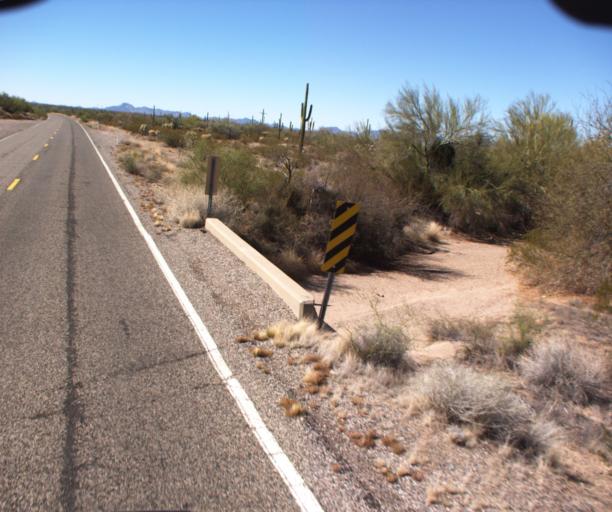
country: US
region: Arizona
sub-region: Pima County
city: Ajo
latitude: 32.2266
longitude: -112.7551
